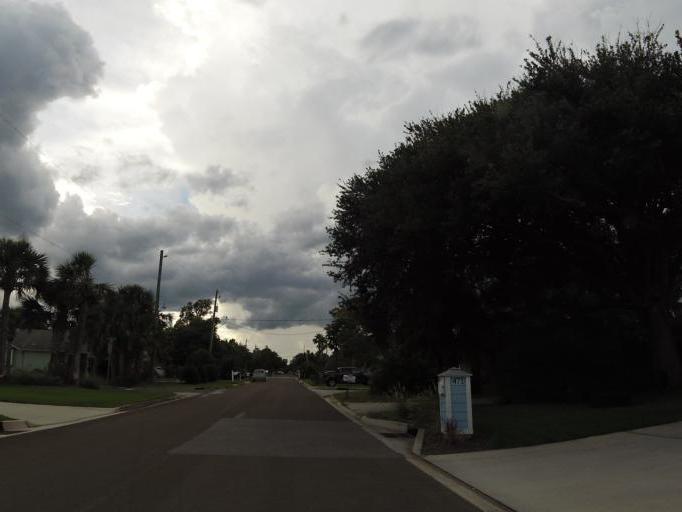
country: US
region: Florida
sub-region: Duval County
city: Jacksonville Beach
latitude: 30.2739
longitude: -81.3908
